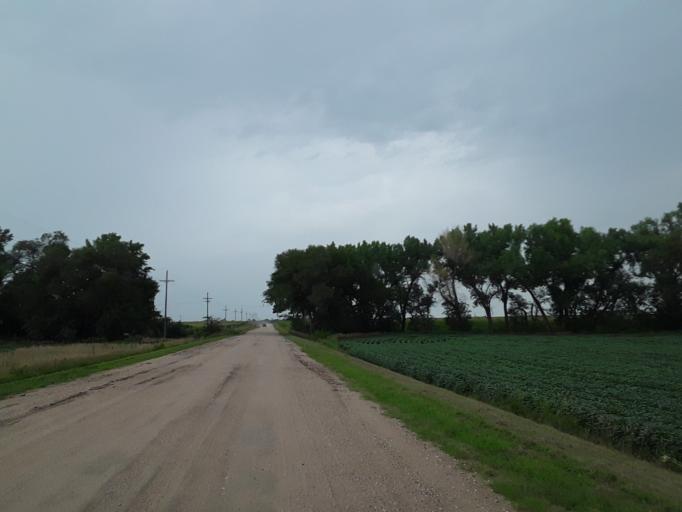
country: US
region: Nebraska
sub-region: Saunders County
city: Yutan
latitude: 41.1663
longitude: -96.4448
